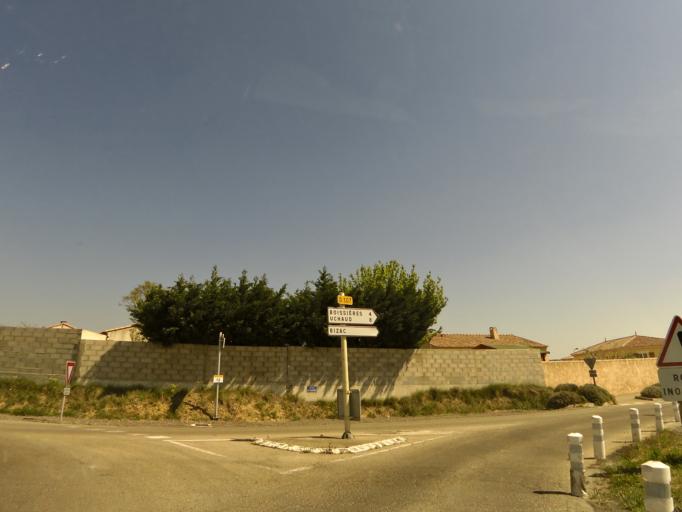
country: FR
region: Languedoc-Roussillon
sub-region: Departement du Gard
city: Calvisson
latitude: 43.7818
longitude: 4.2061
